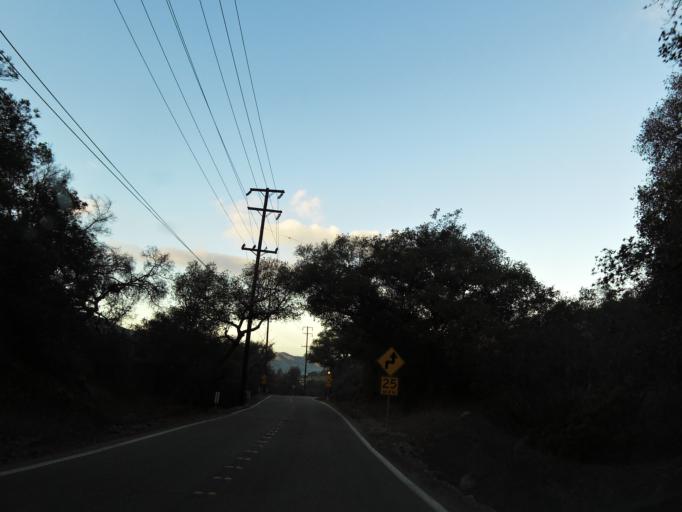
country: US
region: California
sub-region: Ventura County
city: Casa Conejo
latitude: 34.1569
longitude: -118.9350
